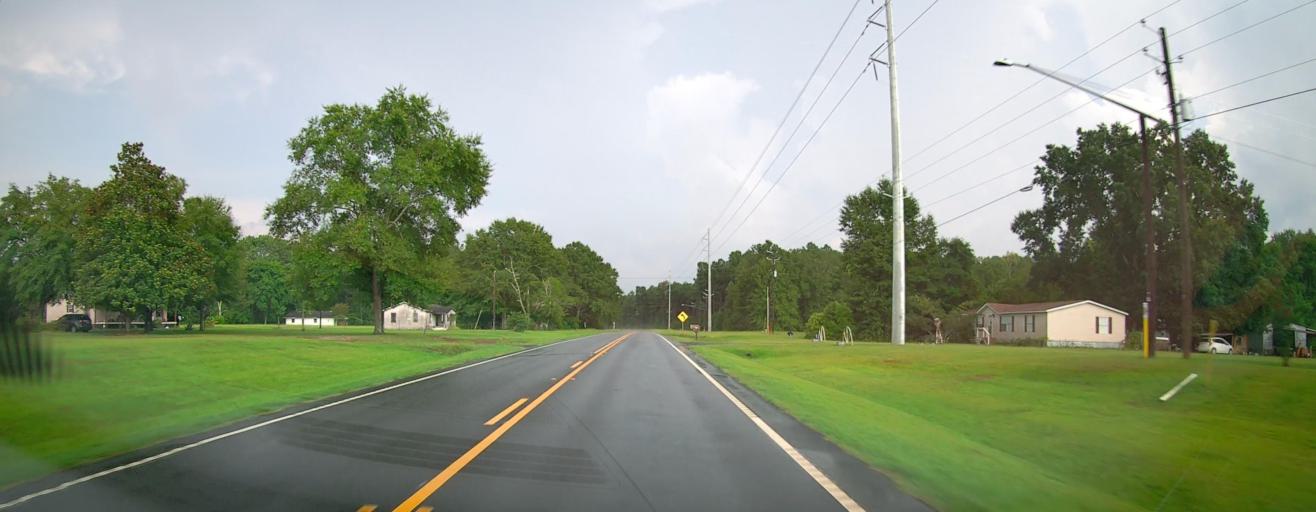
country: US
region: Georgia
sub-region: Twiggs County
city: Jeffersonville
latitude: 32.5861
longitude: -83.2224
